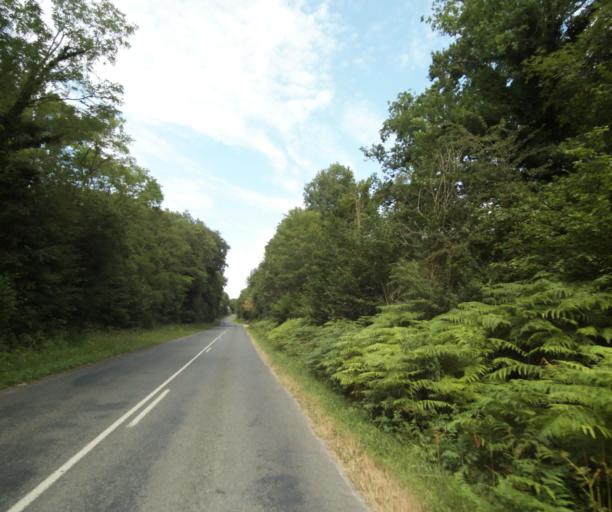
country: FR
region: Ile-de-France
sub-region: Departement de Seine-et-Marne
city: Chailly-en-Biere
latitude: 48.4848
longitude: 2.6279
